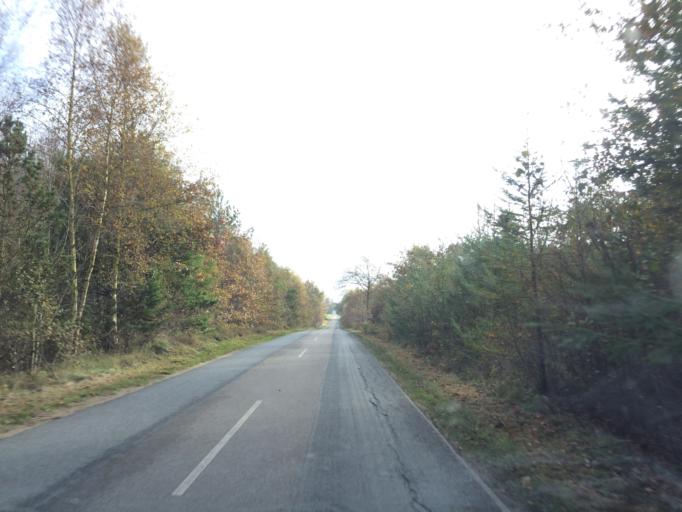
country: DK
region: Central Jutland
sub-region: Holstebro Kommune
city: Holstebro
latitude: 56.3517
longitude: 8.5570
